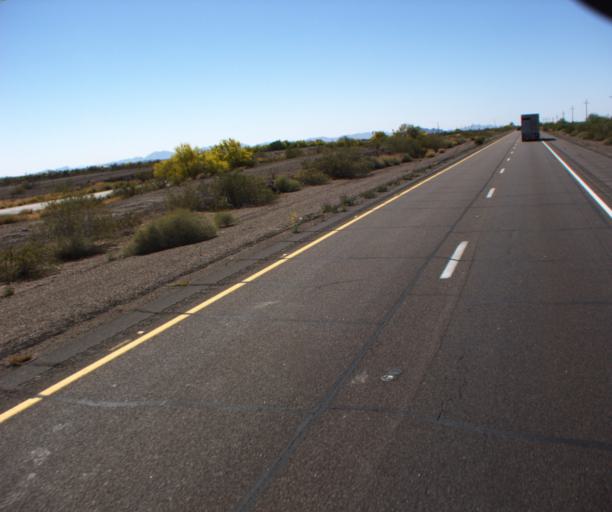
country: US
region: Arizona
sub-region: Maricopa County
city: Gila Bend
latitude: 32.8401
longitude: -113.3240
